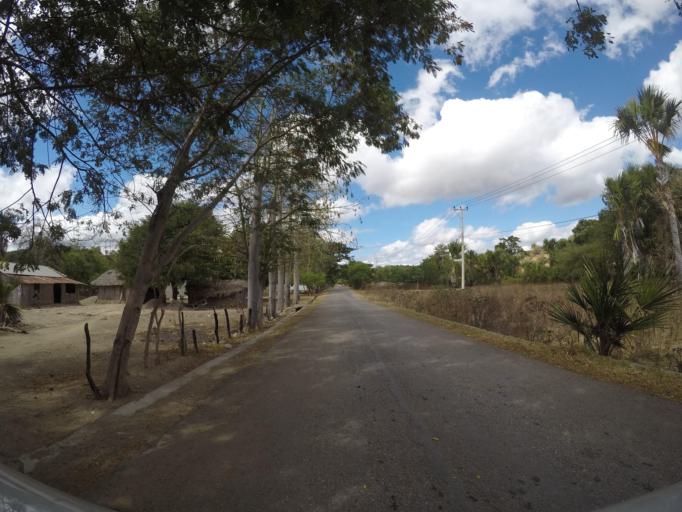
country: TL
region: Lautem
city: Lospalos
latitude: -8.4045
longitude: 126.8301
